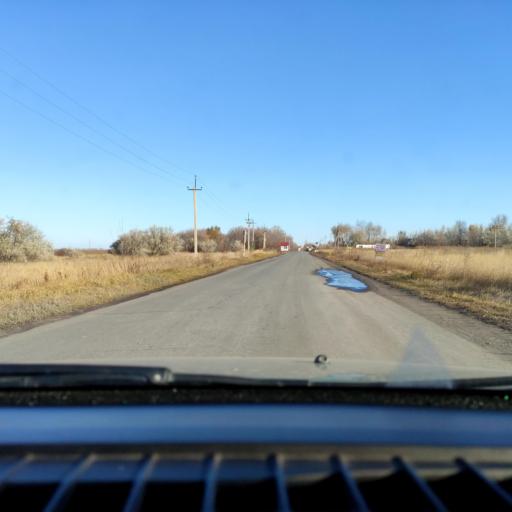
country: RU
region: Samara
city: Tol'yatti
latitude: 53.6577
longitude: 49.3316
